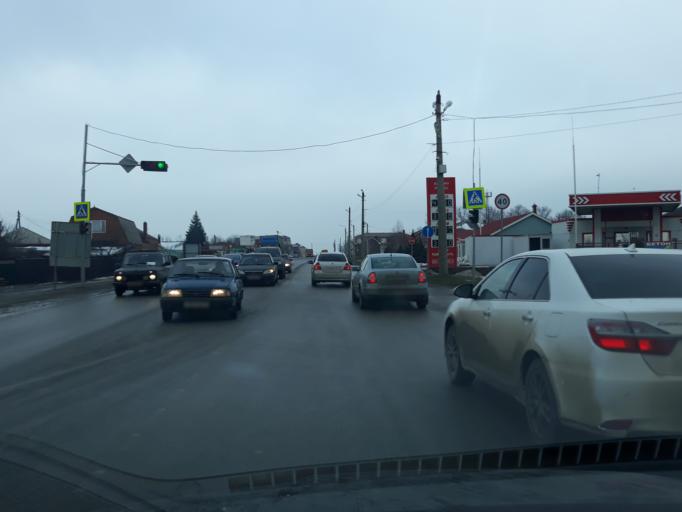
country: RU
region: Rostov
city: Krym
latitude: 47.2772
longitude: 39.5091
